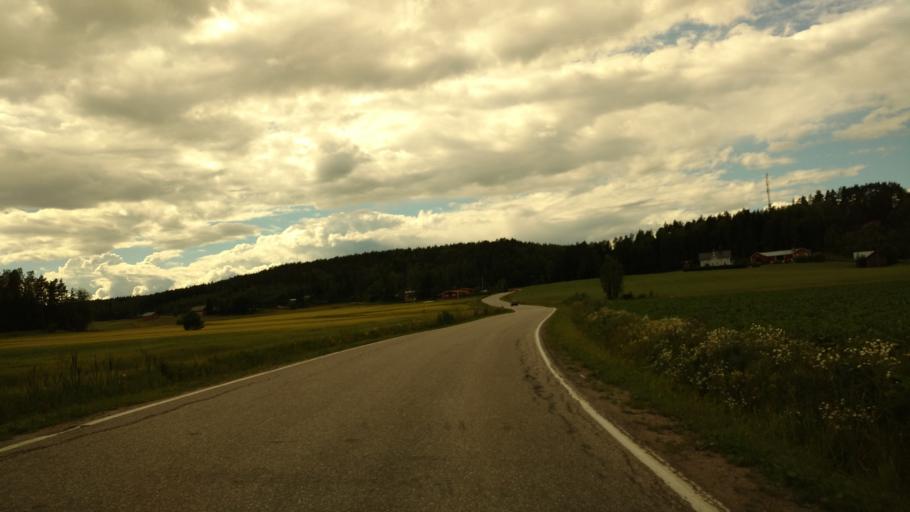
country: FI
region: Varsinais-Suomi
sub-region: Salo
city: Halikko
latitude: 60.3992
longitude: 23.0270
